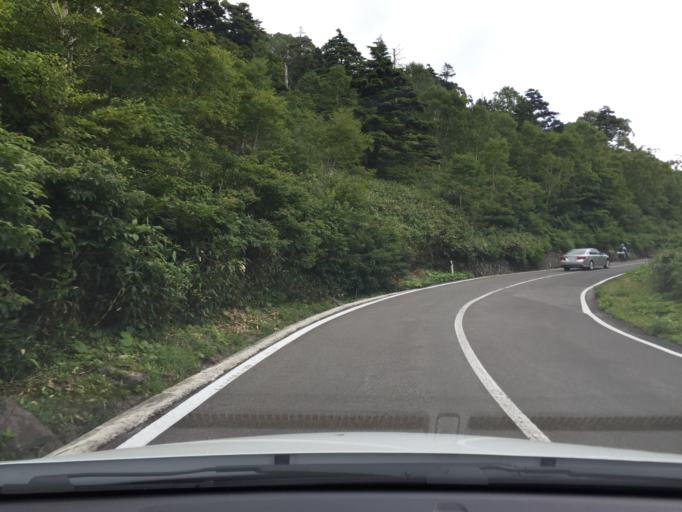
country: JP
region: Fukushima
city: Inawashiro
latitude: 37.6920
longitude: 140.2368
